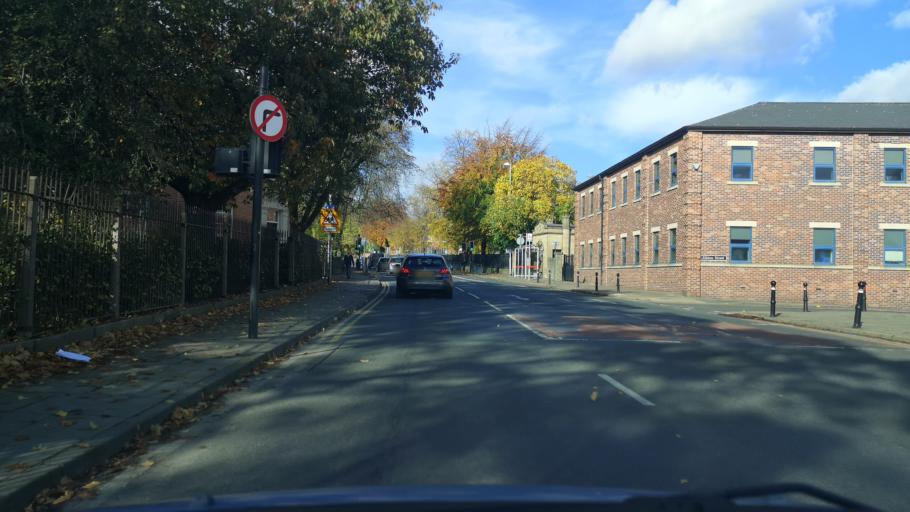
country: GB
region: England
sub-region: City and Borough of Wakefield
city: Wakefield
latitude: 53.6875
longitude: -1.5015
